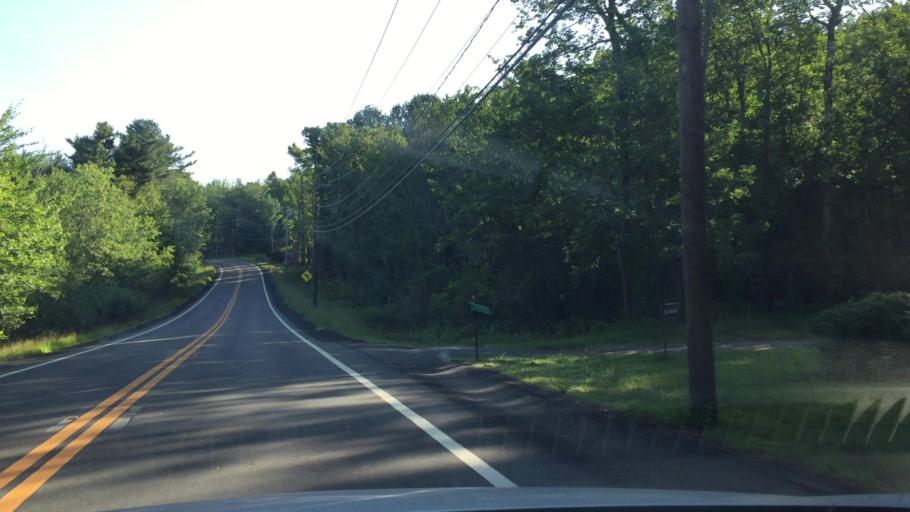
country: US
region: Massachusetts
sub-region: Berkshire County
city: Becket
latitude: 42.2905
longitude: -73.0589
